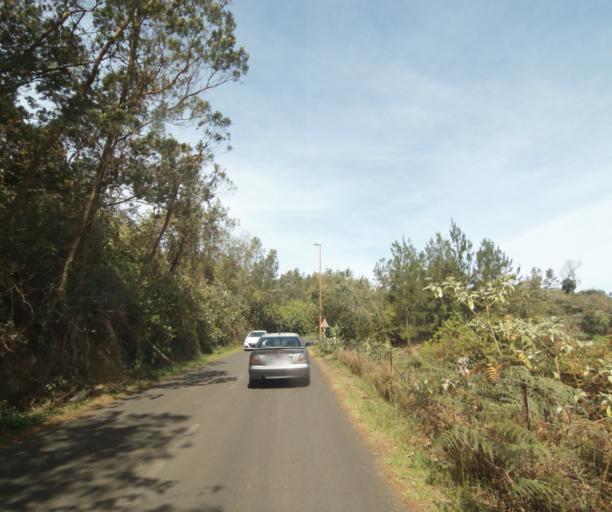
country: RE
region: Reunion
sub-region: Reunion
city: Trois-Bassins
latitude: -21.0480
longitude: 55.3339
